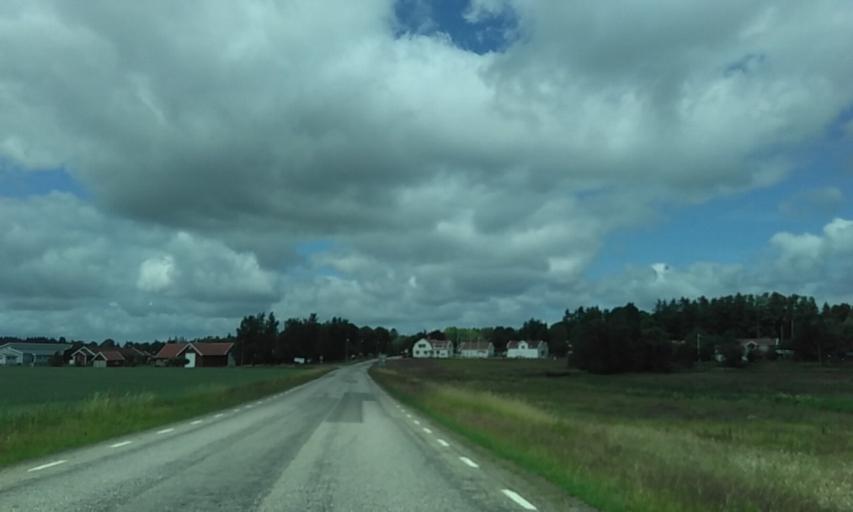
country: SE
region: Vaestra Goetaland
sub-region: Vargarda Kommun
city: Vargarda
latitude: 58.1234
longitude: 12.7847
